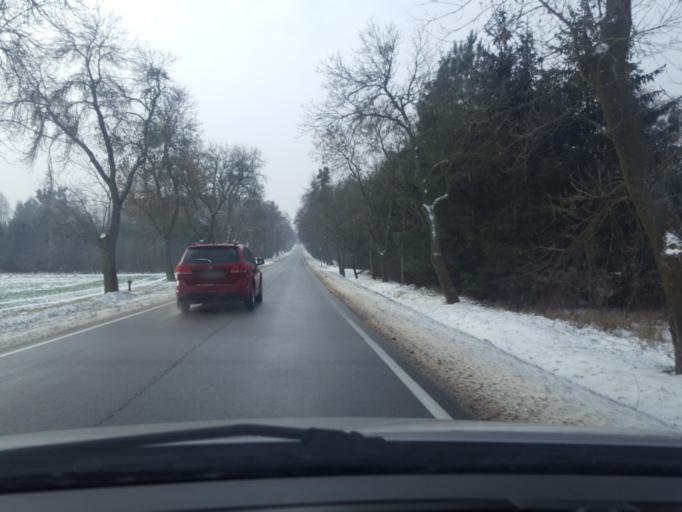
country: PL
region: Lodz Voivodeship
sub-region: Powiat brzezinski
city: Brzeziny
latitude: 51.8290
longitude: 19.7871
